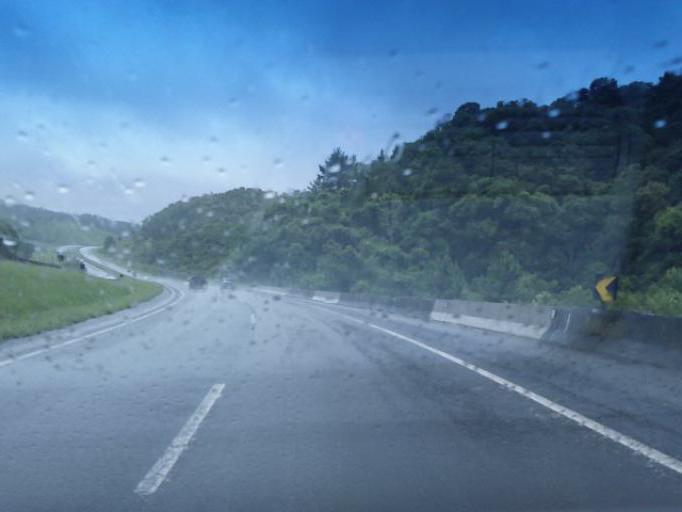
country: BR
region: Parana
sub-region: Campina Grande Do Sul
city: Campina Grande do Sul
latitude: -25.2429
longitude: -48.9024
